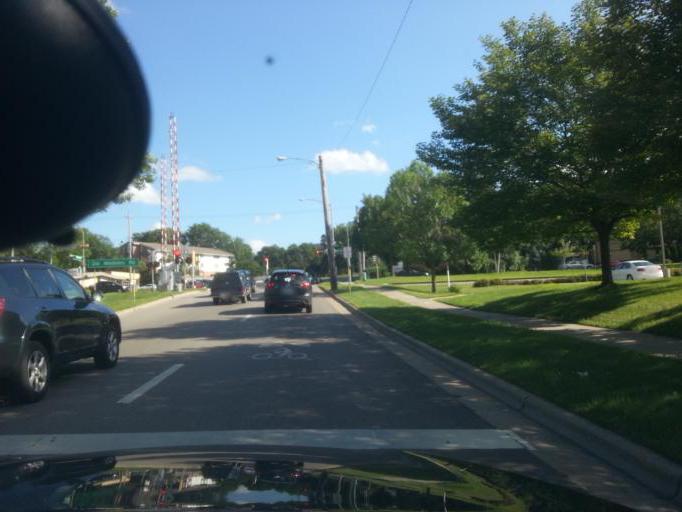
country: US
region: Wisconsin
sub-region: Dane County
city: Shorewood Hills
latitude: 43.0748
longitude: -89.4678
